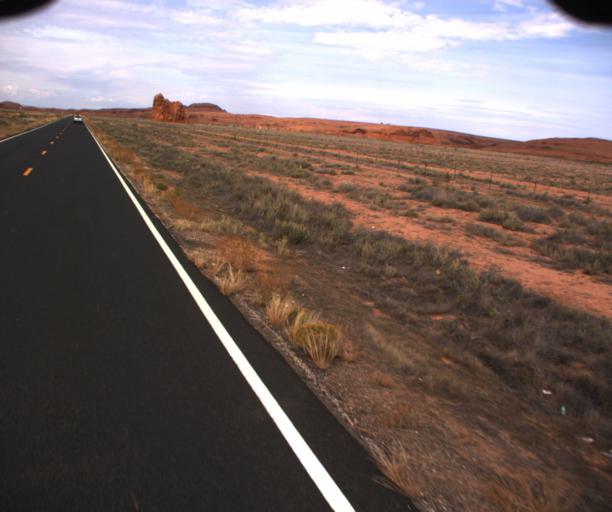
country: US
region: Arizona
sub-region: Apache County
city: Many Farms
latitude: 36.7405
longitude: -109.6367
